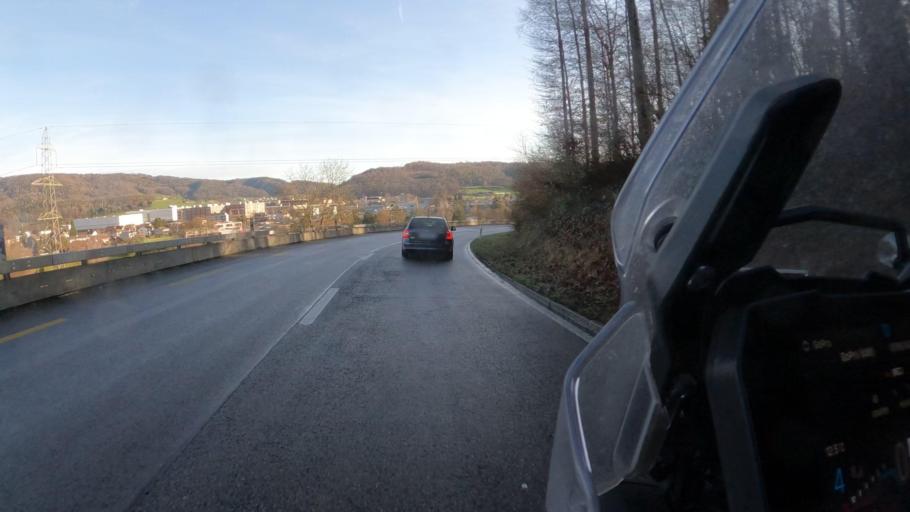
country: CH
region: Zurich
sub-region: Bezirk Buelach
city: Embrach / Kellersacker
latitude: 47.5154
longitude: 8.5818
